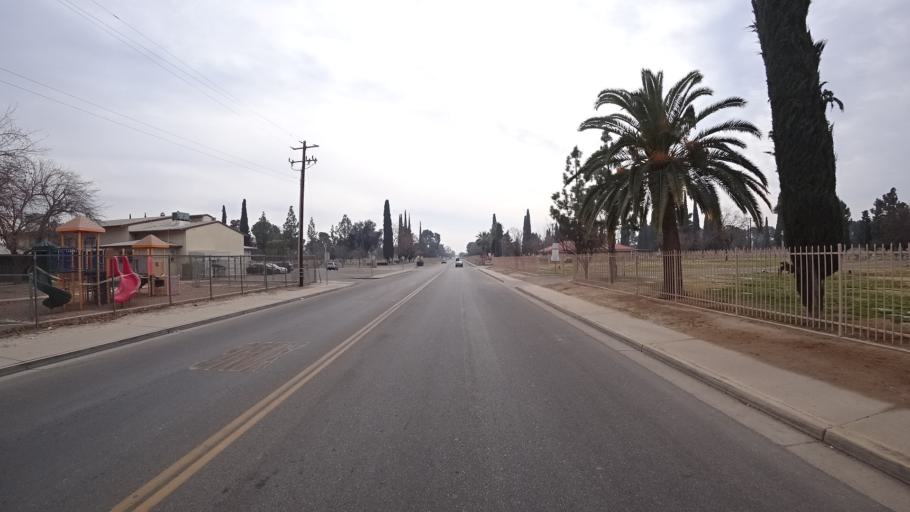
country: US
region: California
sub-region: Kern County
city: Bakersfield
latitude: 35.3656
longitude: -118.9942
